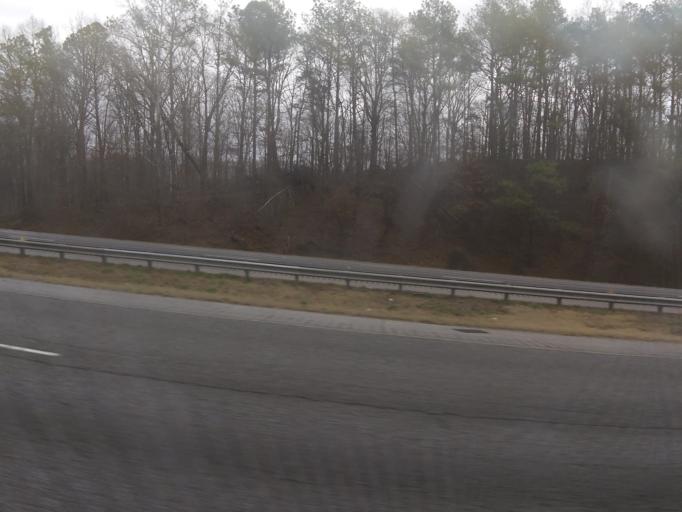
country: US
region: Georgia
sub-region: Gordon County
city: Calhoun
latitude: 34.5916
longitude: -84.9544
